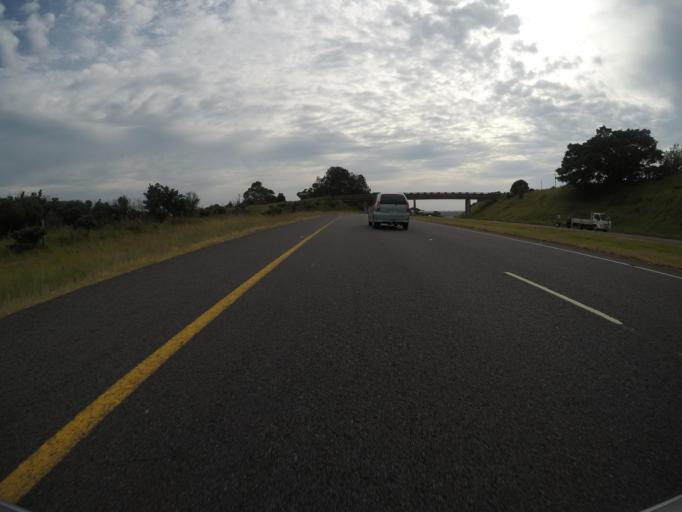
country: ZA
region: Eastern Cape
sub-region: Buffalo City Metropolitan Municipality
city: East London
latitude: -32.9685
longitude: 27.8736
